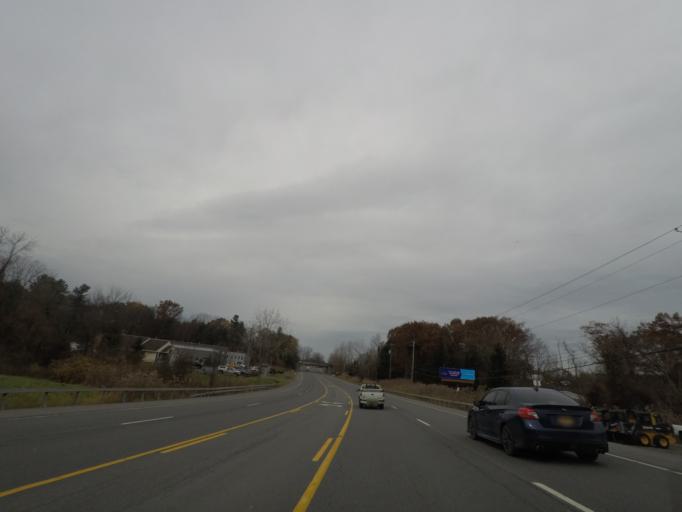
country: US
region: New York
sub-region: Saratoga County
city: Country Knolls
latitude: 42.9025
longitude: -73.7738
